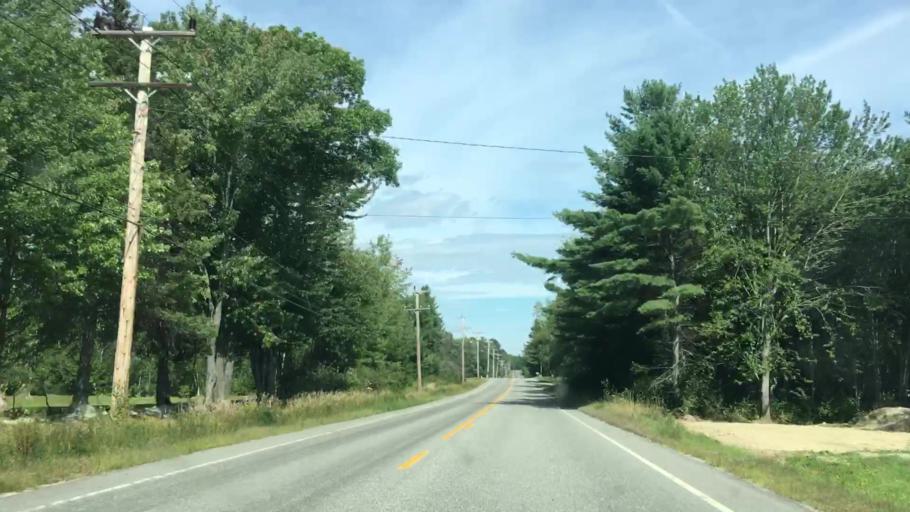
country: US
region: Maine
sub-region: Penobscot County
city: Lincoln
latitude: 45.4282
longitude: -68.4754
